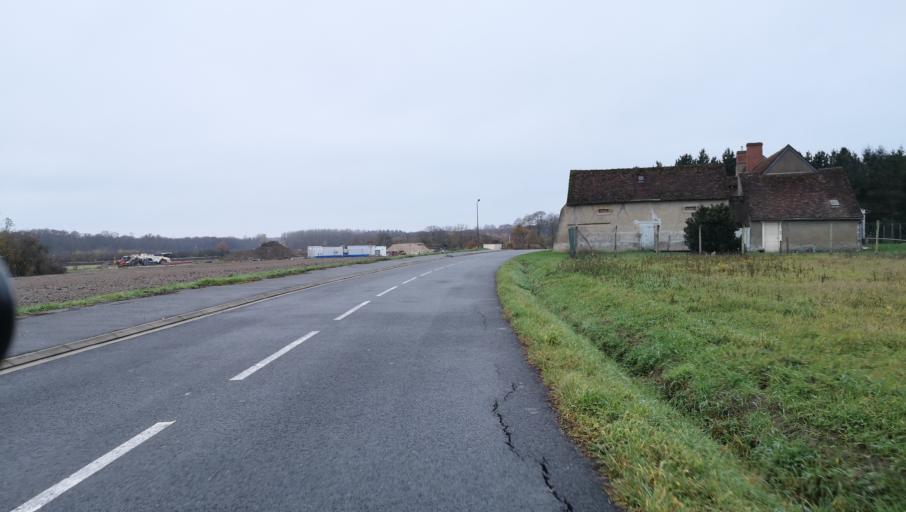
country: FR
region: Centre
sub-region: Departement du Loiret
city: Marigny-les-Usages
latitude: 47.9503
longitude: 2.0107
